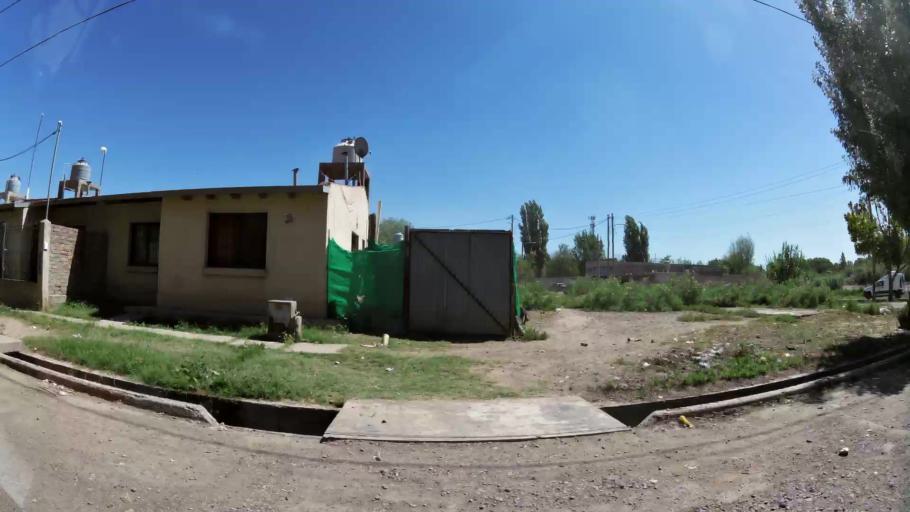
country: AR
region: Mendoza
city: Villa Nueva
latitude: -32.8720
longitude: -68.7841
